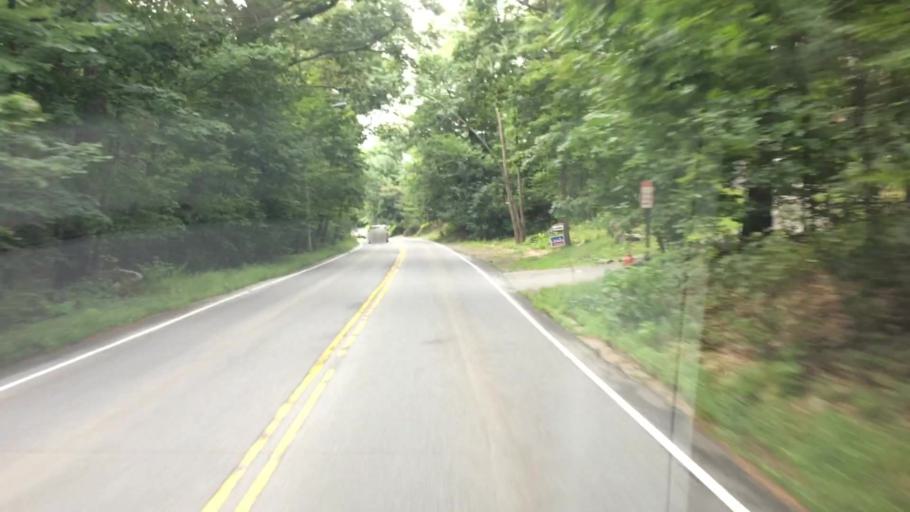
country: US
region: Massachusetts
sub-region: Middlesex County
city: Winchester
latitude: 42.4467
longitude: -71.1253
